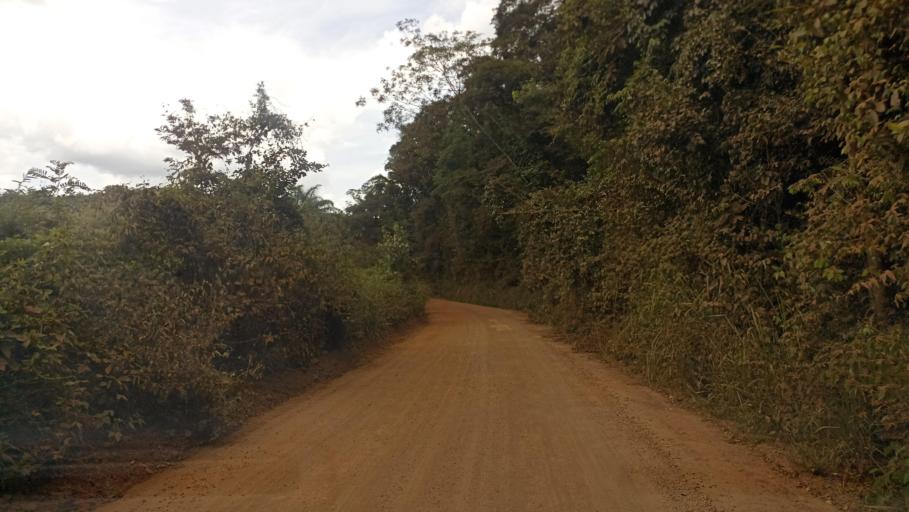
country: BR
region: Minas Gerais
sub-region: Itabirito
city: Itabirito
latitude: -20.3573
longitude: -43.7695
